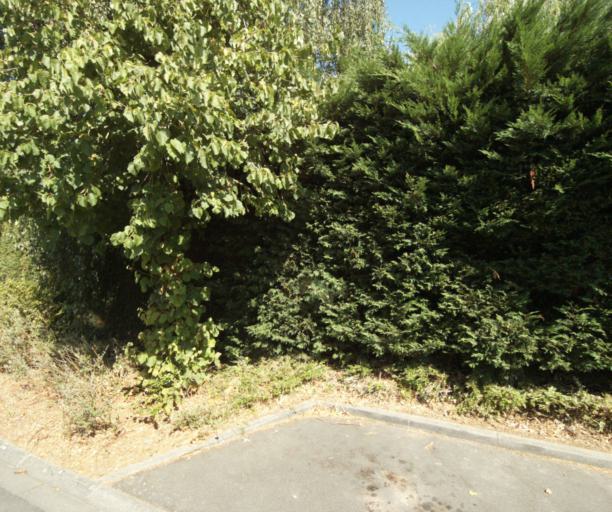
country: FR
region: Nord-Pas-de-Calais
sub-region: Departement du Nord
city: Halluin
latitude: 50.7721
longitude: 3.1175
